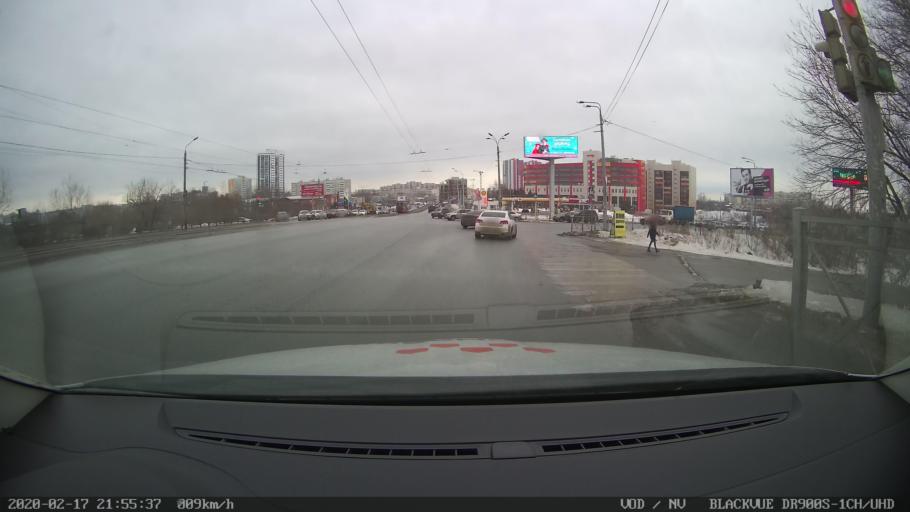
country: RU
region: Tatarstan
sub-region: Gorod Kazan'
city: Kazan
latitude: 55.7758
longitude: 49.1767
